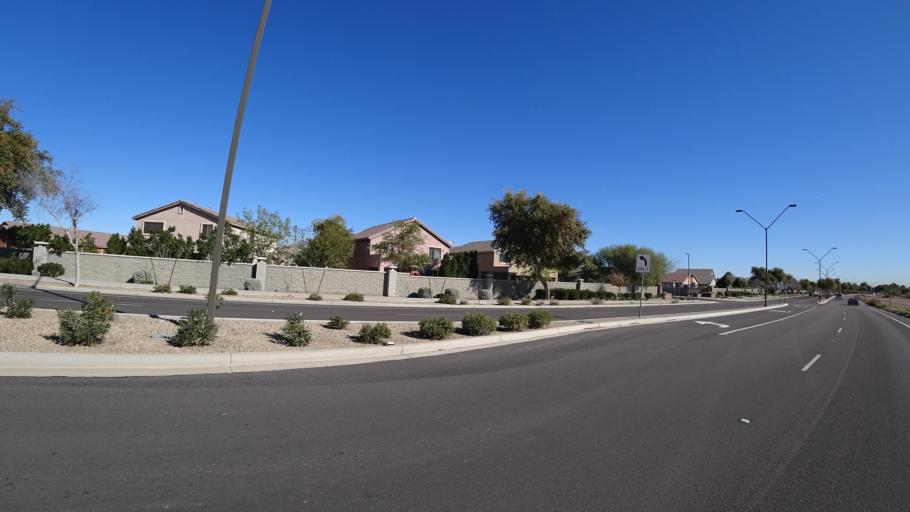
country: US
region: Arizona
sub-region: Maricopa County
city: Litchfield Park
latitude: 33.4753
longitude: -112.3905
